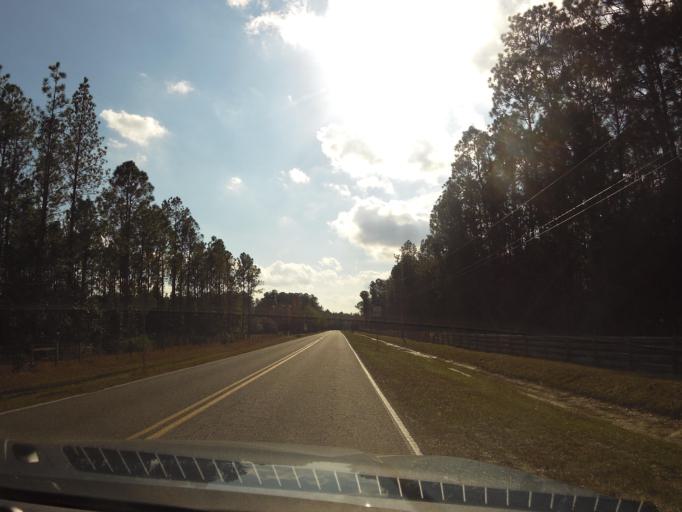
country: US
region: Florida
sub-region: Duval County
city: Baldwin
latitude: 30.1572
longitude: -82.0011
